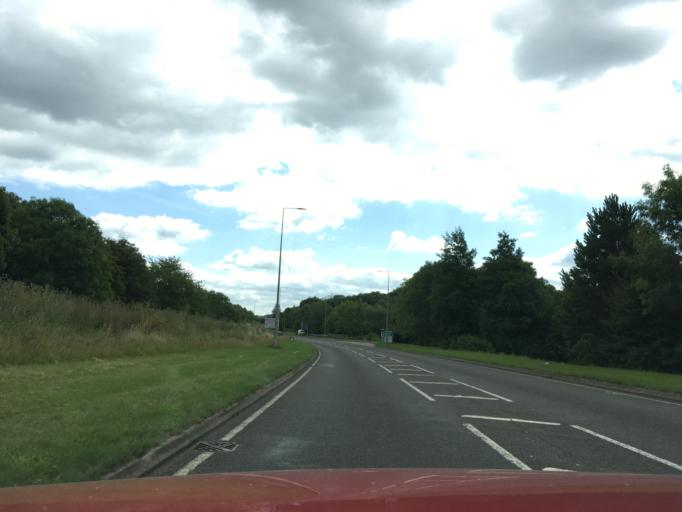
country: GB
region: England
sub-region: Milton Keynes
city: Shenley Church End
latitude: 52.0214
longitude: -0.8022
